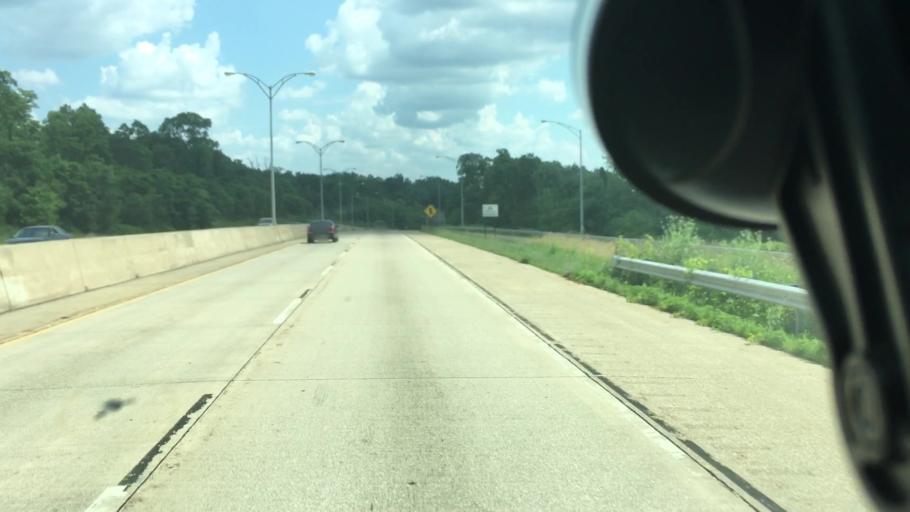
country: US
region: Ohio
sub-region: Trumbull County
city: Churchill
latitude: 41.1311
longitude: -80.6757
